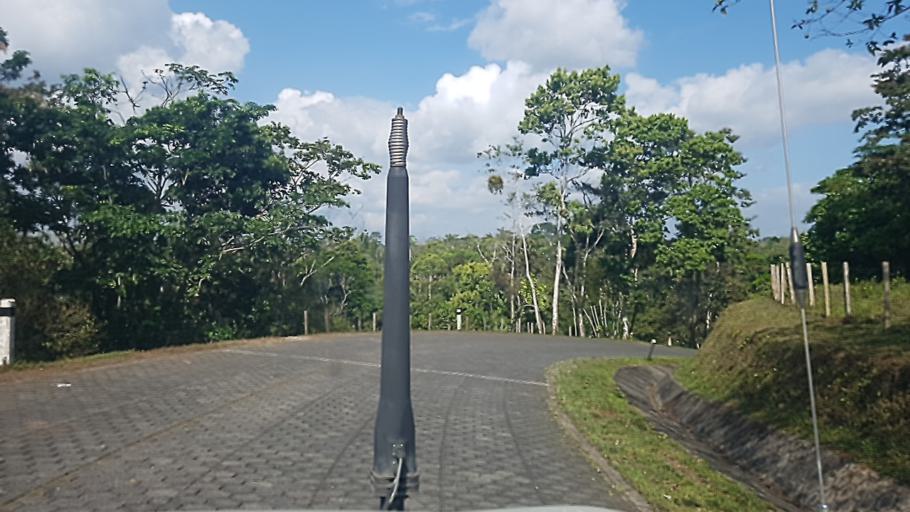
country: NI
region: Atlantico Sur
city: Nueva Guinea
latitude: 11.6985
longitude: -84.3958
